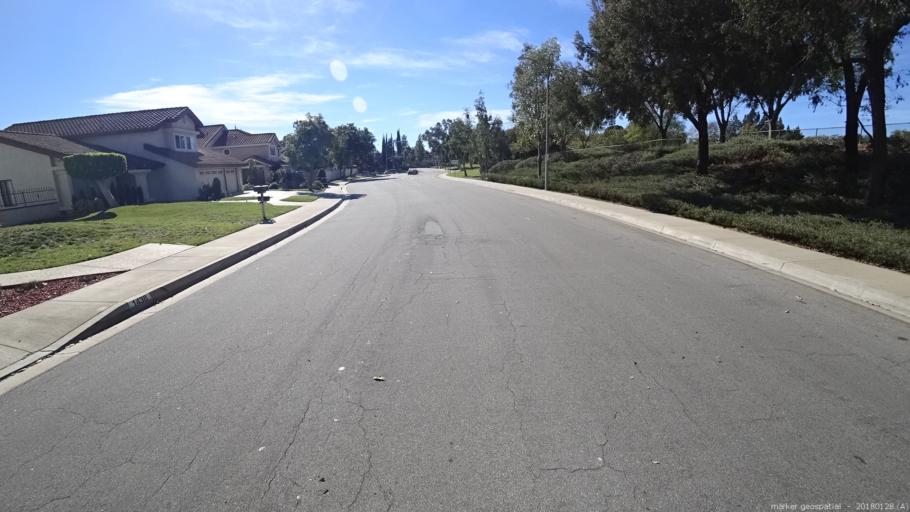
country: US
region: California
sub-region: Los Angeles County
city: Diamond Bar
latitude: 33.9971
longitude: -117.7977
